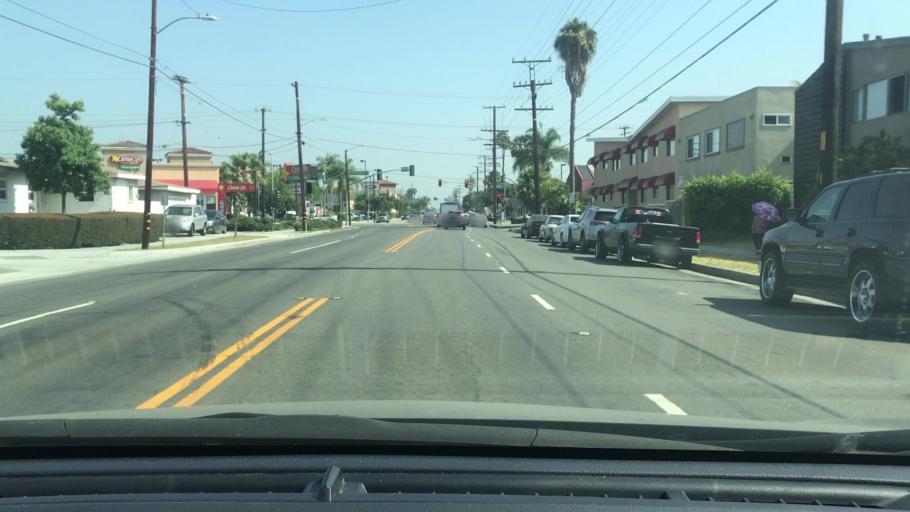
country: US
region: California
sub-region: Los Angeles County
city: Gardena
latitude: 33.8845
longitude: -118.3178
